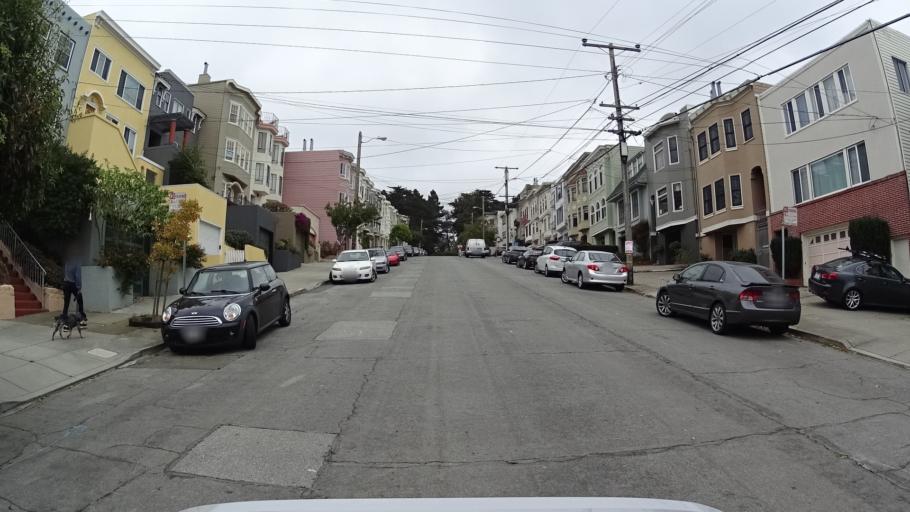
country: US
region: California
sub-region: San Francisco County
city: San Francisco
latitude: 37.7743
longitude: -122.4800
